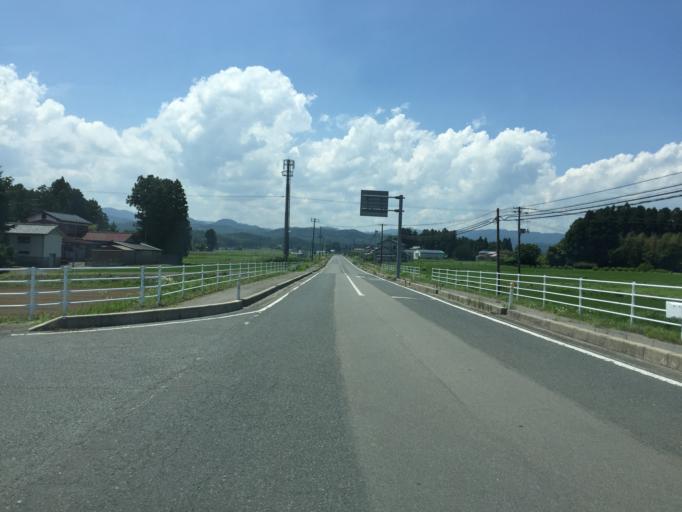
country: JP
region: Fukushima
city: Namie
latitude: 37.7121
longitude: 140.9543
